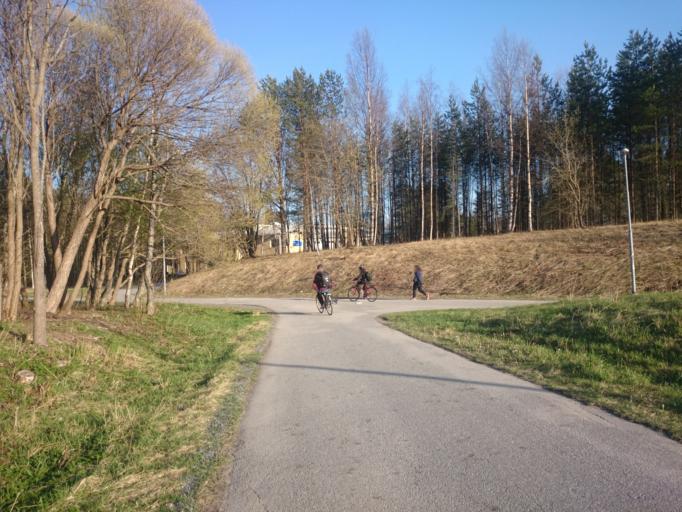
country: SE
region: Vaesterbotten
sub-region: Umea Kommun
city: Umea
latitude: 63.8159
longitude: 20.3152
